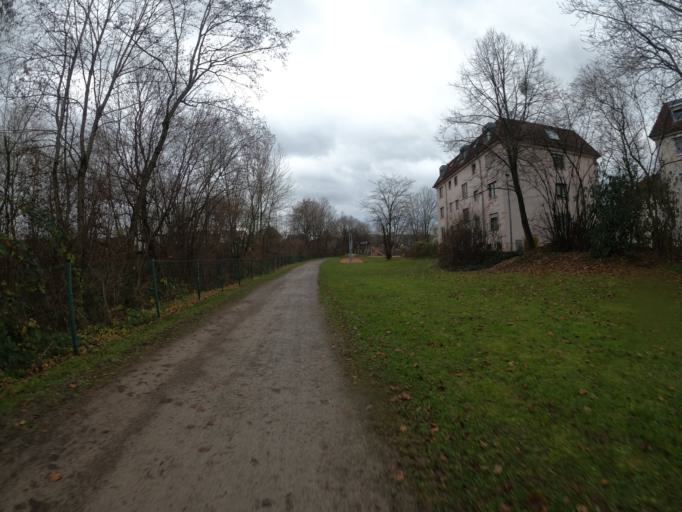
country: DE
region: Baden-Wuerttemberg
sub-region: Regierungsbezirk Stuttgart
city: Sussen
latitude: 48.6846
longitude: 9.7523
